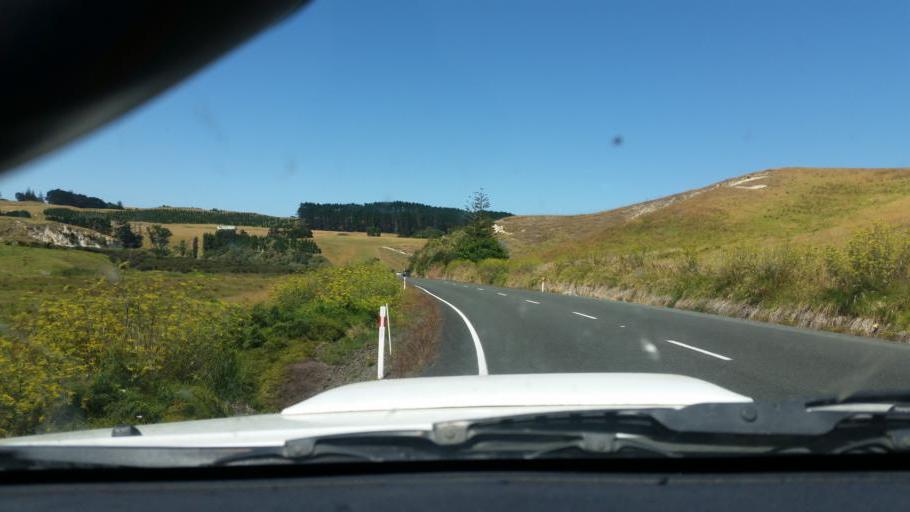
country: NZ
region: Northland
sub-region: Kaipara District
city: Dargaville
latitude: -35.8319
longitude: 173.6636
